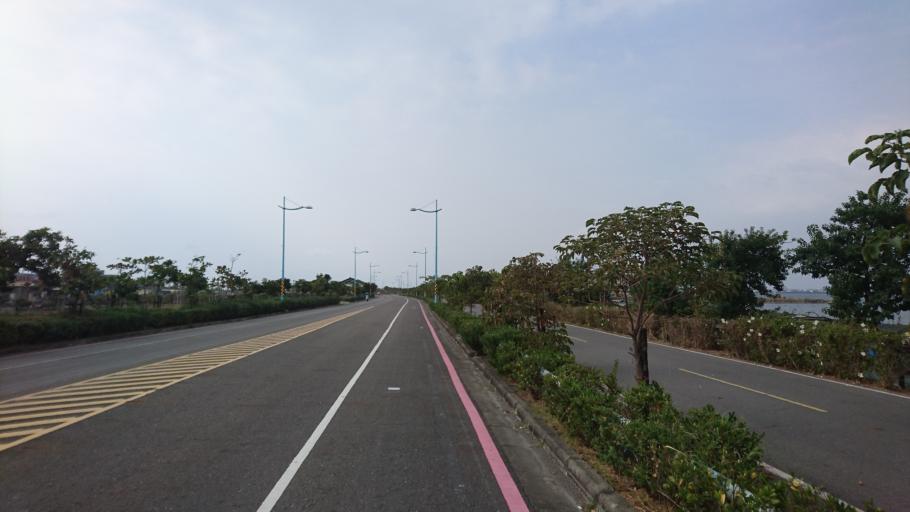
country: TW
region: Taiwan
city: Fengshan
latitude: 22.4335
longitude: 120.4828
